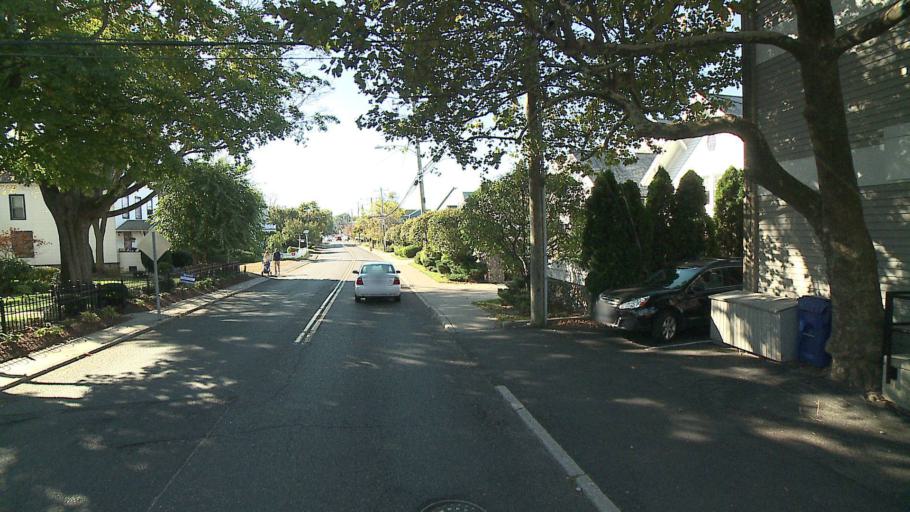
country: US
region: Connecticut
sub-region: Fairfield County
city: Darien
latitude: 41.0672
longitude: -73.4438
